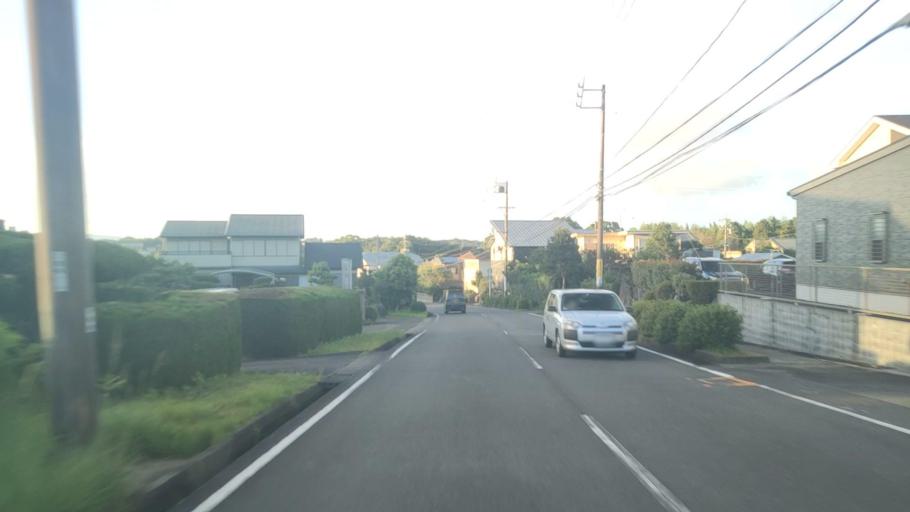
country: JP
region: Mie
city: Toba
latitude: 34.3252
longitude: 136.8223
